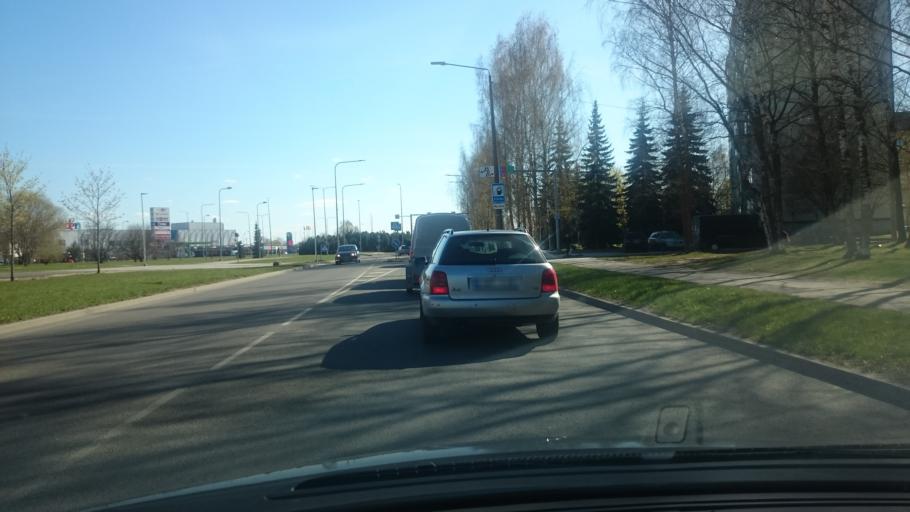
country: EE
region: Tartu
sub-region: Tartu linn
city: Tartu
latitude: 58.3763
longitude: 26.7502
